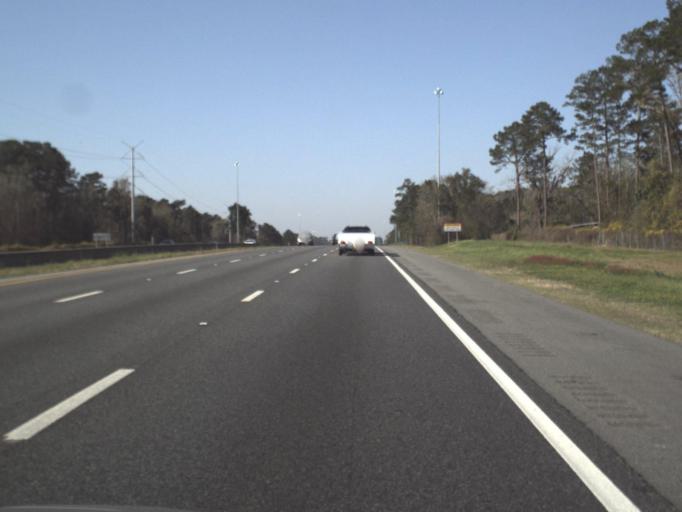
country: US
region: Florida
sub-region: Leon County
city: Tallahassee
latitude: 30.4906
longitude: -84.2848
